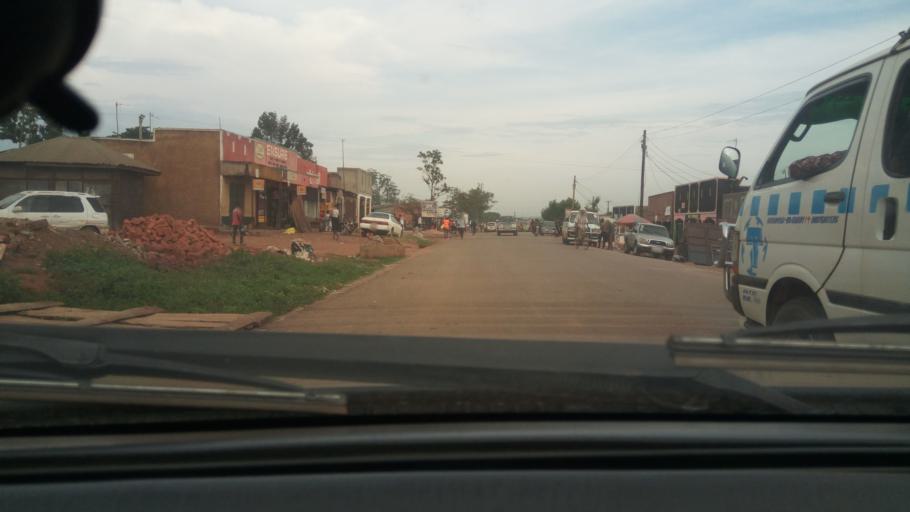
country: UG
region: Central Region
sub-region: Mityana District
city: Mityana
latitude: 0.5669
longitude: 32.2024
